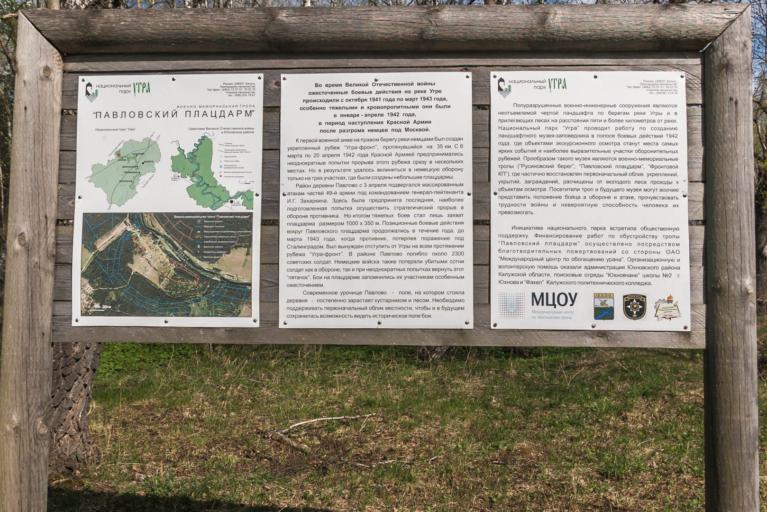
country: RU
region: Kaluga
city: Yukhnov
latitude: 54.8386
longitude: 34.9988
